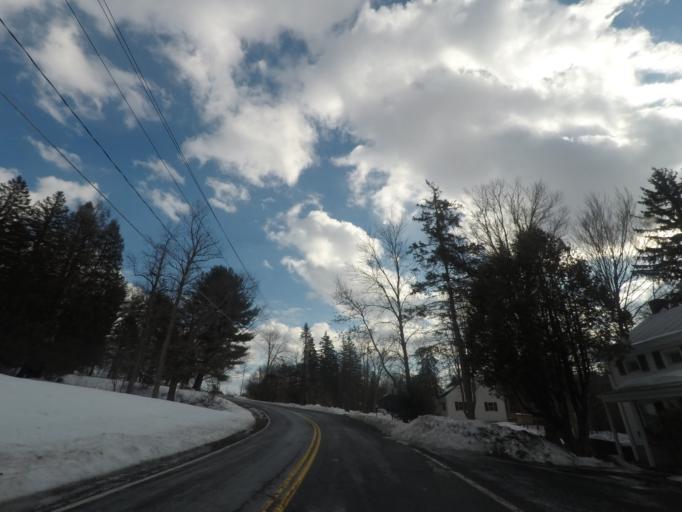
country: US
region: New York
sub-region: Schenectady County
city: Niskayuna
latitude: 42.8156
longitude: -73.8479
